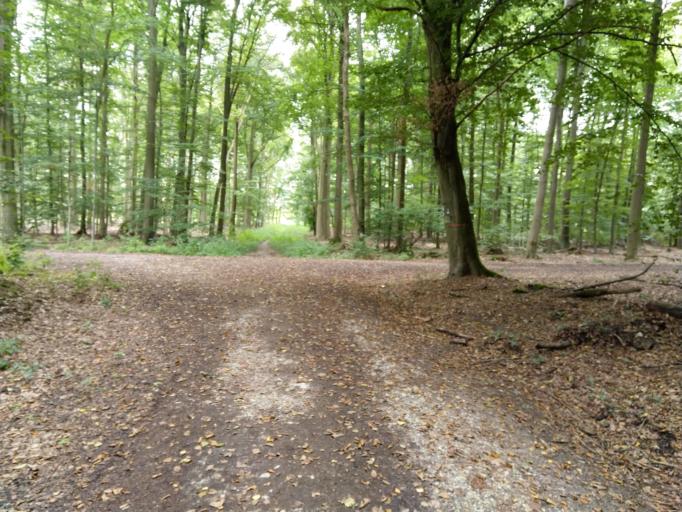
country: DE
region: North Rhine-Westphalia
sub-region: Regierungsbezirk Detmold
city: Leopoldshohe
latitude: 52.0416
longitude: 8.7015
